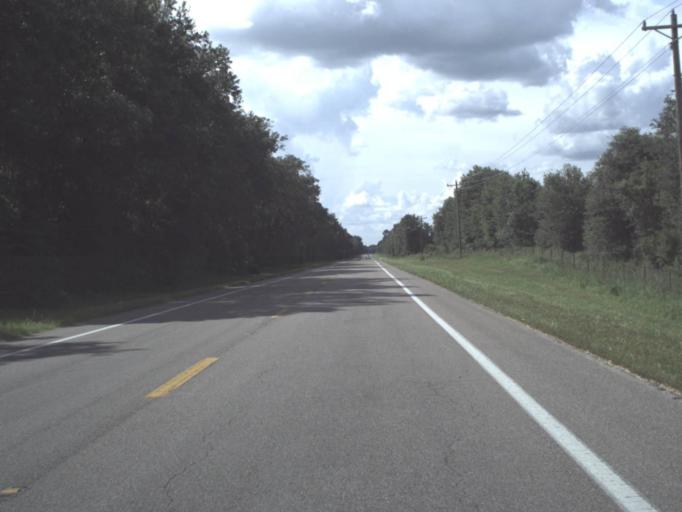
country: US
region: Florida
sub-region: Gilchrist County
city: Trenton
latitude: 29.6497
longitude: -82.8382
